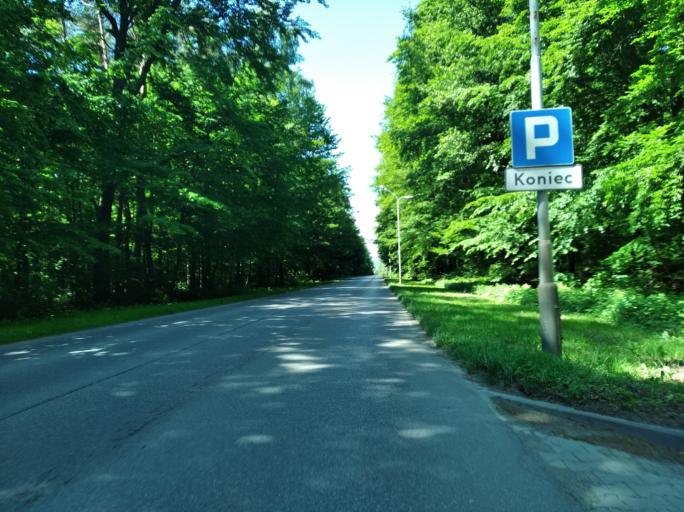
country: PL
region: Subcarpathian Voivodeship
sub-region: Powiat krosnienski
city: Jedlicze
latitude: 49.7260
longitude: 21.6690
